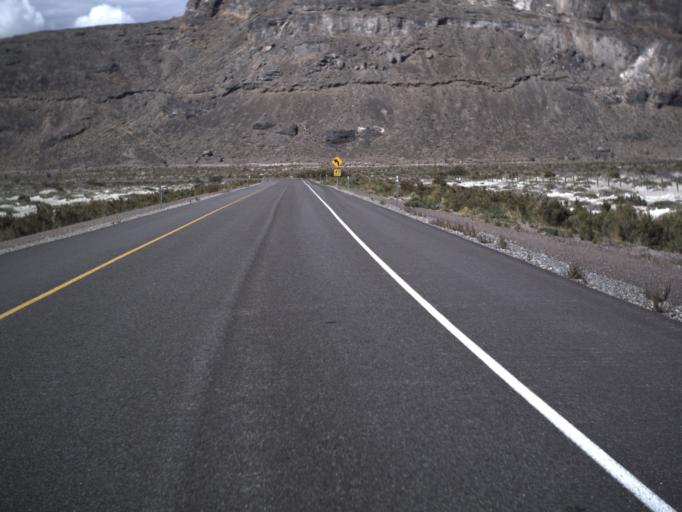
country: US
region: Utah
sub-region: Tooele County
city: Wendover
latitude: 40.7478
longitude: -114.0063
